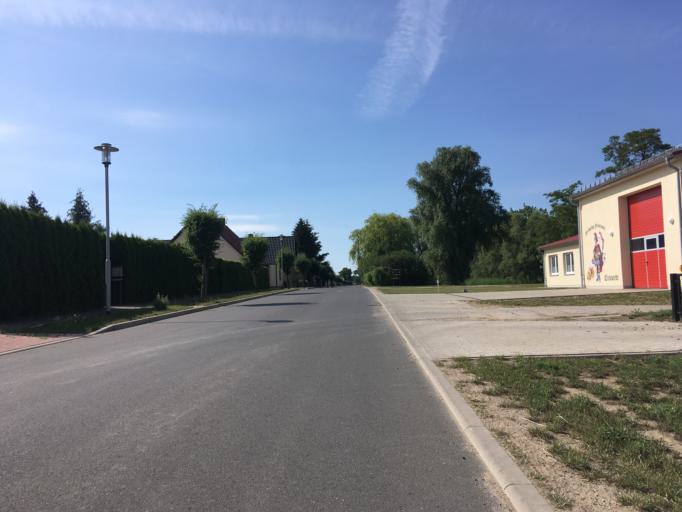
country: DE
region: Brandenburg
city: Grunow
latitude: 53.3024
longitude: 14.0407
